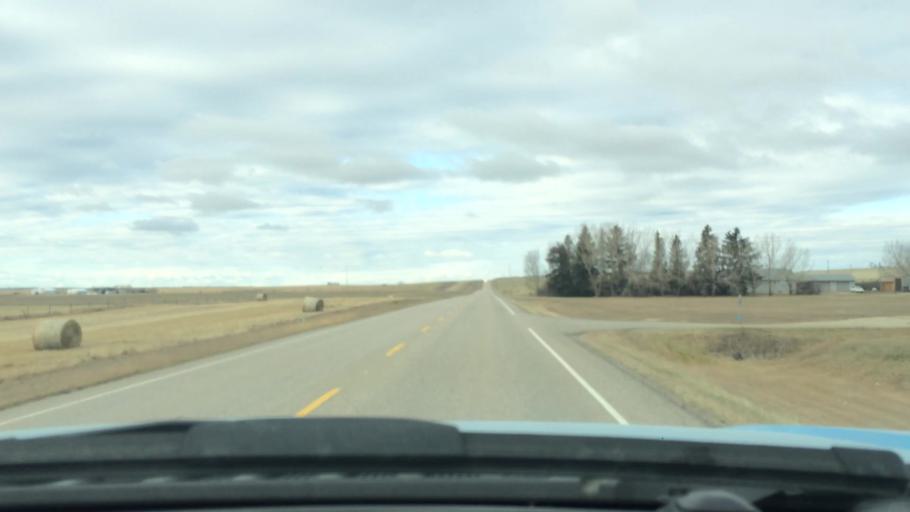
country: CA
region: Alberta
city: Airdrie
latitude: 51.2125
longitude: -114.0898
